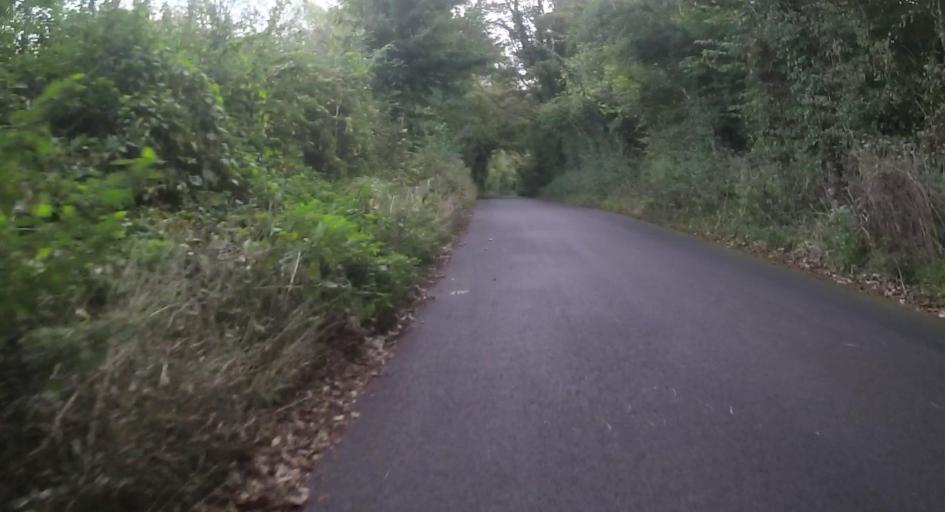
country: GB
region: England
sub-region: Hampshire
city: Tadley
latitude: 51.4019
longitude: -1.1831
